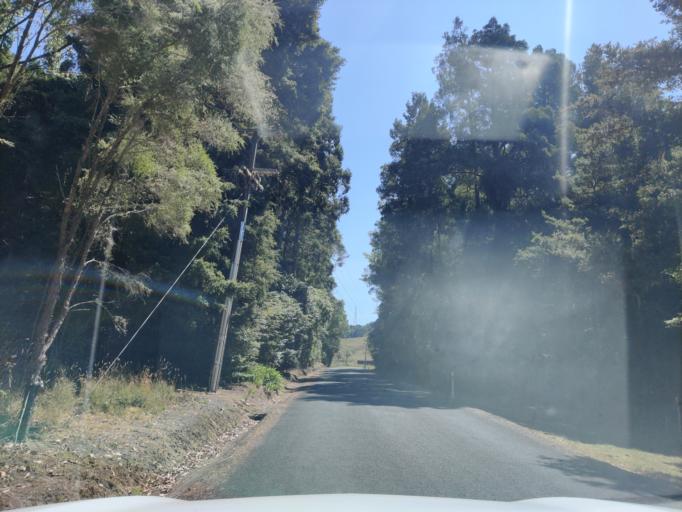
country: NZ
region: Auckland
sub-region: Auckland
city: Red Hill
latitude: -37.0650
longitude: 175.0870
